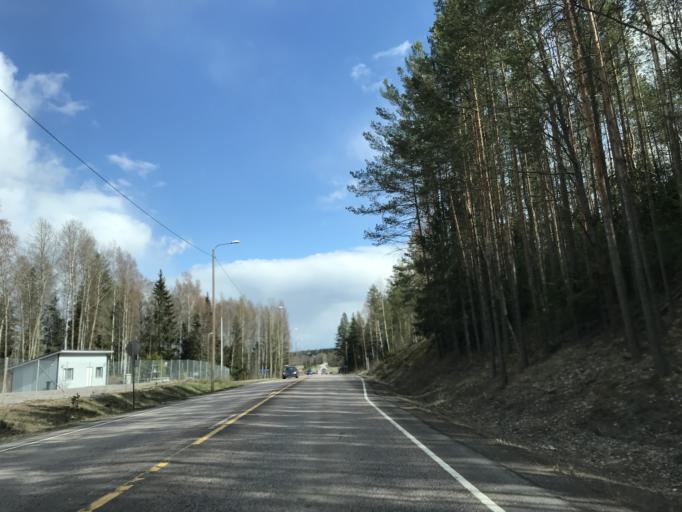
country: FI
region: Uusimaa
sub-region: Helsinki
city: Hyvinge
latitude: 60.5400
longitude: 24.8926
